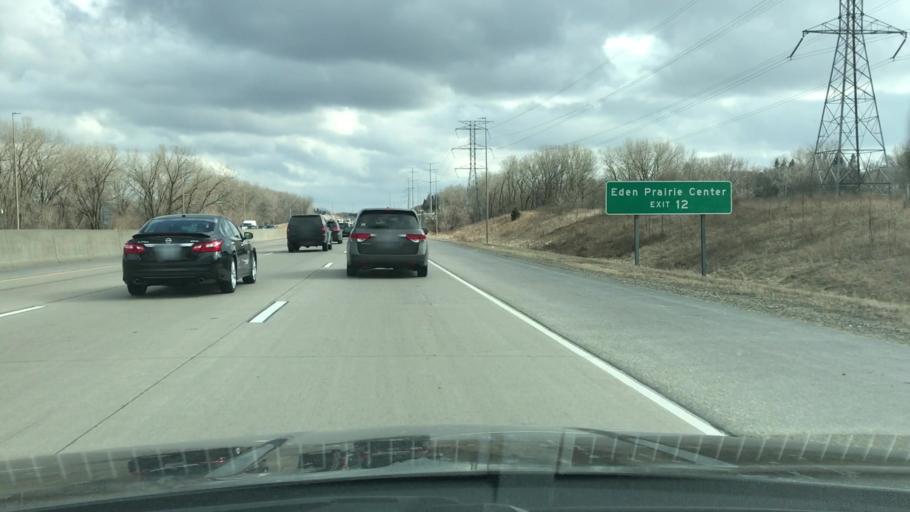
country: US
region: Minnesota
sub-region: Hennepin County
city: Eden Prairie
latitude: 44.8794
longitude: -93.4378
